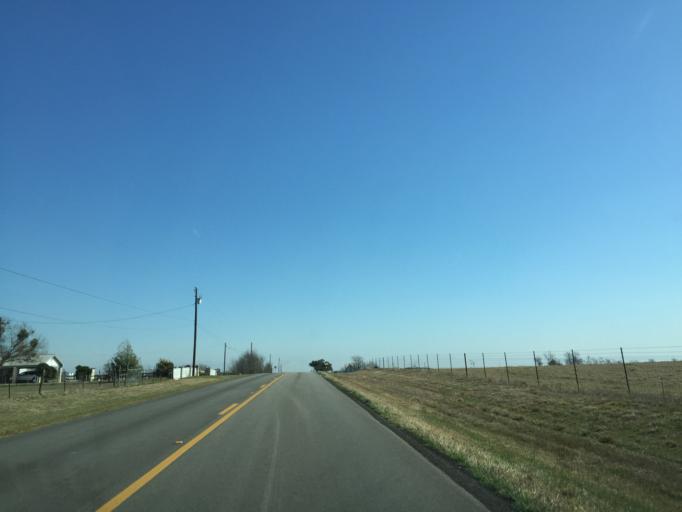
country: US
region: Texas
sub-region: Williamson County
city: Serenada
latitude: 30.7321
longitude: -97.6157
